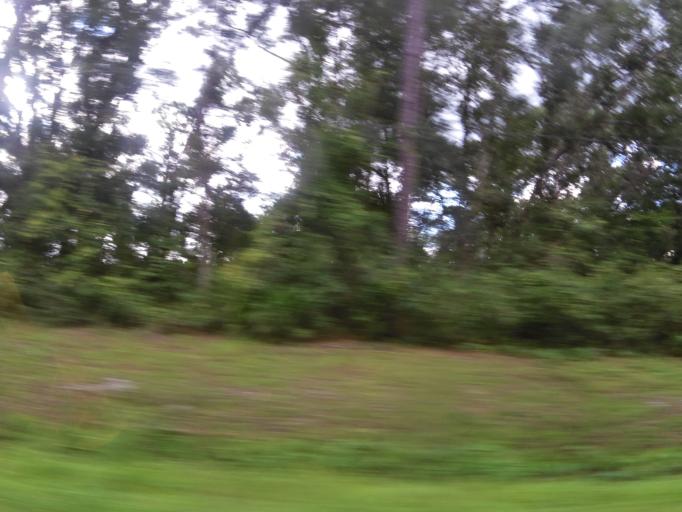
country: US
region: Florida
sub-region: Putnam County
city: East Palatka
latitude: 29.7697
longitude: -81.4785
